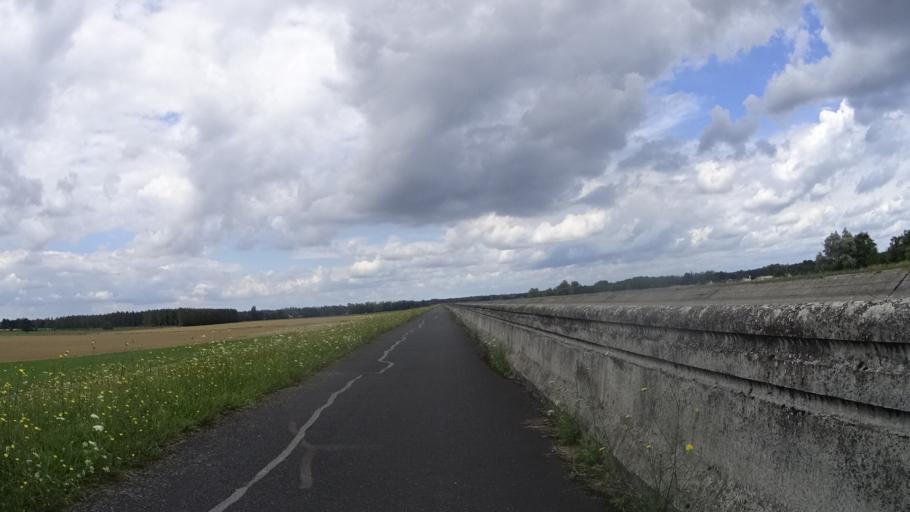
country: FR
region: Champagne-Ardenne
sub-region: Departement de la Haute-Marne
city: Villiers-en-Lieu
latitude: 48.5817
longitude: 4.8522
